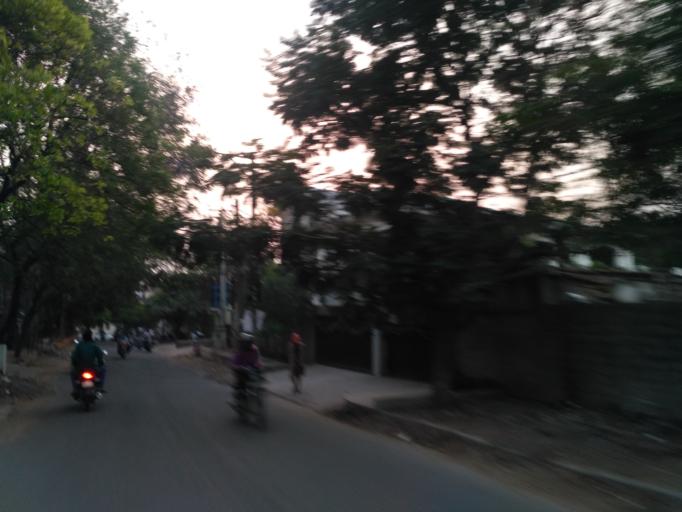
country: IN
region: Telangana
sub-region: Rangareddi
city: Kukatpalli
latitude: 17.4384
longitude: 78.4024
